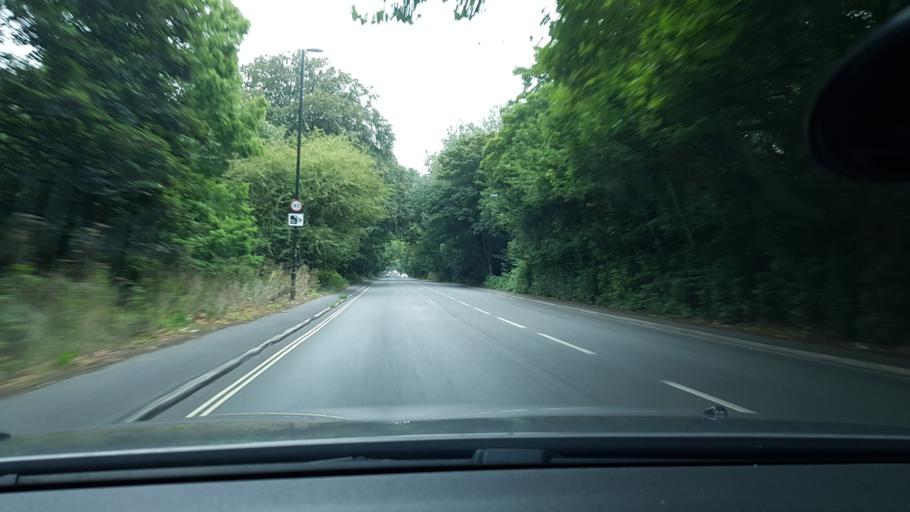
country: GB
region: England
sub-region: Southampton
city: Southampton
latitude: 50.9344
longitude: -1.4062
